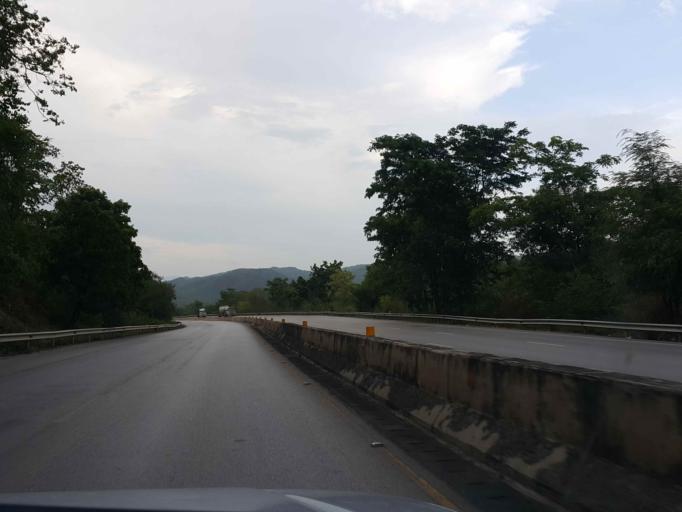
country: TH
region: Lampang
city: Soem Ngam
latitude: 18.0436
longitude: 99.3813
